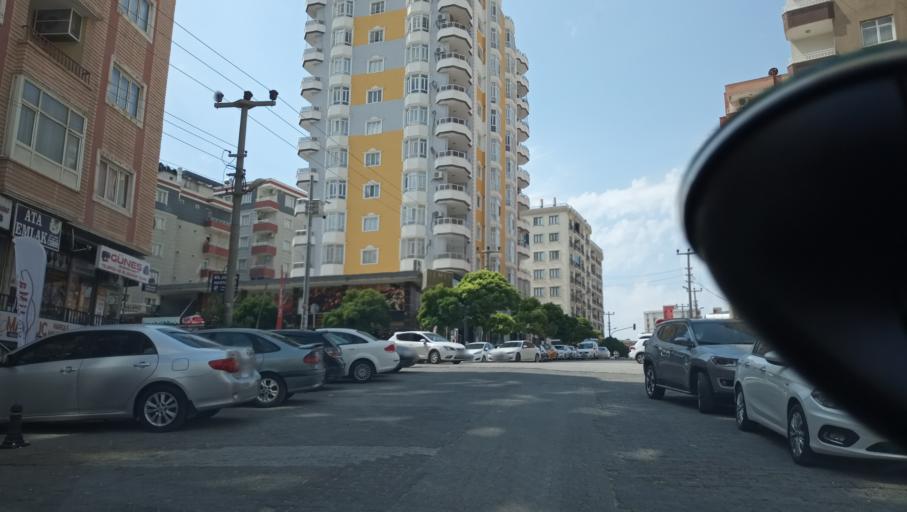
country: TR
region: Mardin
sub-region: Mardin Ilcesi
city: Mardin
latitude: 37.3271
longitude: 40.7175
